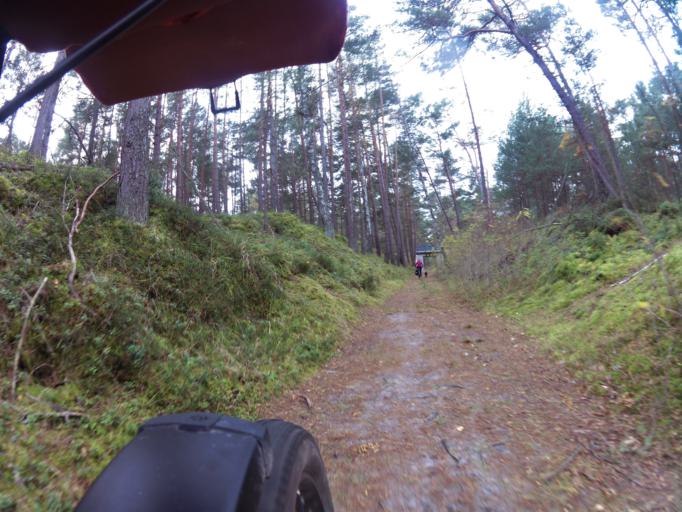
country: PL
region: Pomeranian Voivodeship
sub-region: Powiat pucki
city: Hel
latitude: 54.6280
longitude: 18.8051
